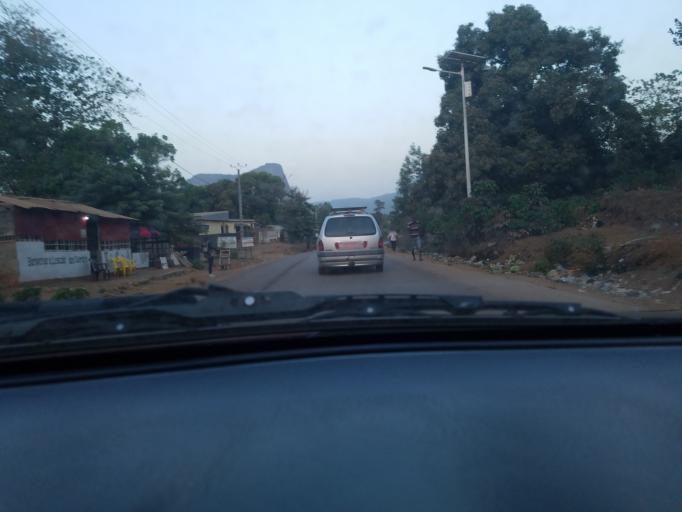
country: GN
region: Kindia
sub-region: Prefecture de Dubreka
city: Dubreka
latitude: 9.7892
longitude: -13.5039
